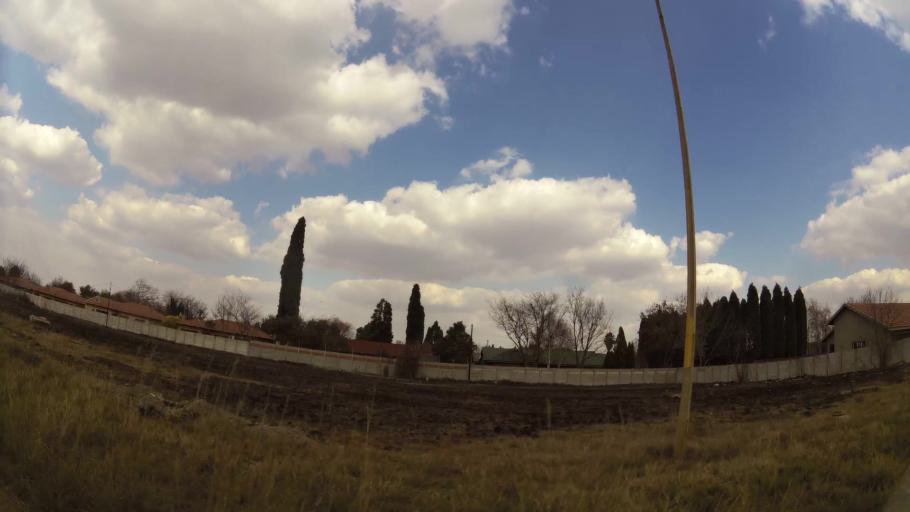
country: ZA
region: Mpumalanga
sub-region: Nkangala District Municipality
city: Delmas
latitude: -26.1357
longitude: 28.6766
